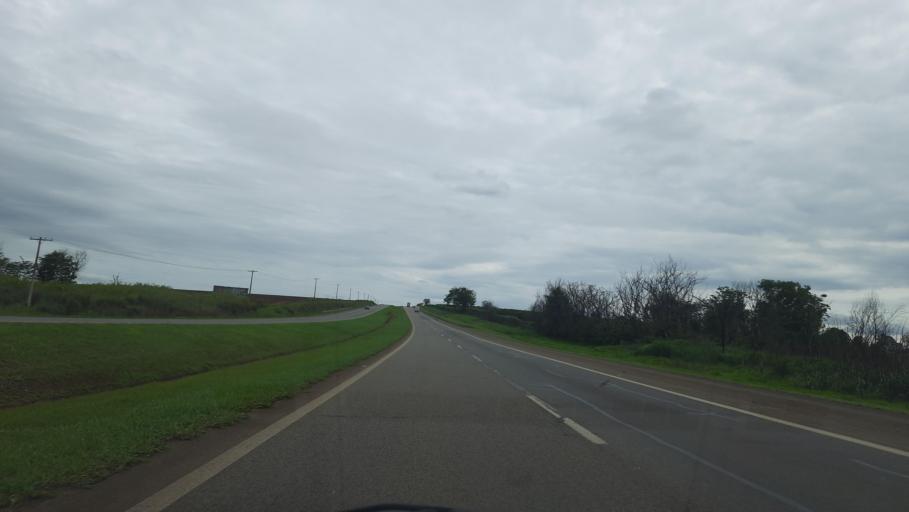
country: BR
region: Sao Paulo
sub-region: Aguai
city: Aguai
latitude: -22.1248
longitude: -47.0012
